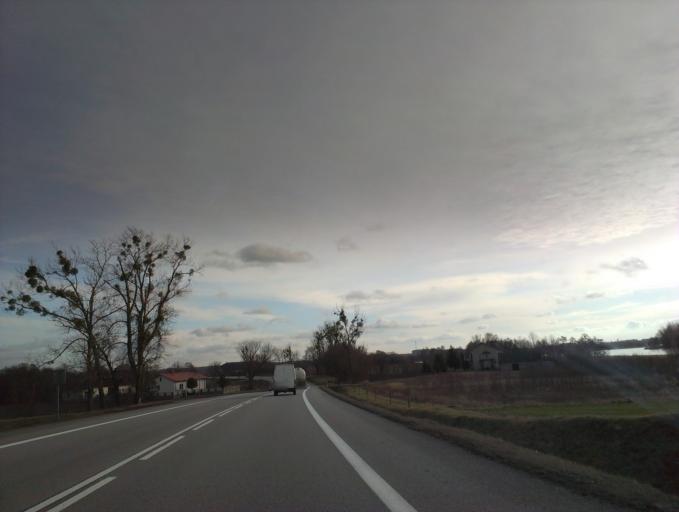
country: PL
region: Kujawsko-Pomorskie
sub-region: Powiat lipnowski
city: Kikol
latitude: 52.9214
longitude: 19.0955
